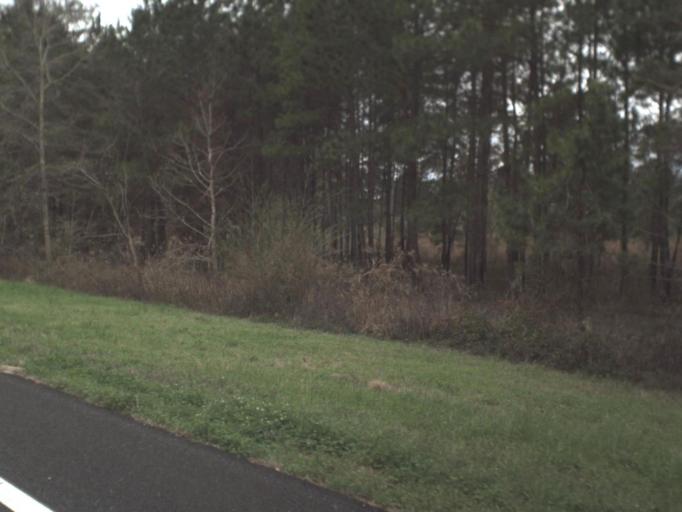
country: US
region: Florida
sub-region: Leon County
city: Tallahassee
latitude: 30.6084
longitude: -84.1779
